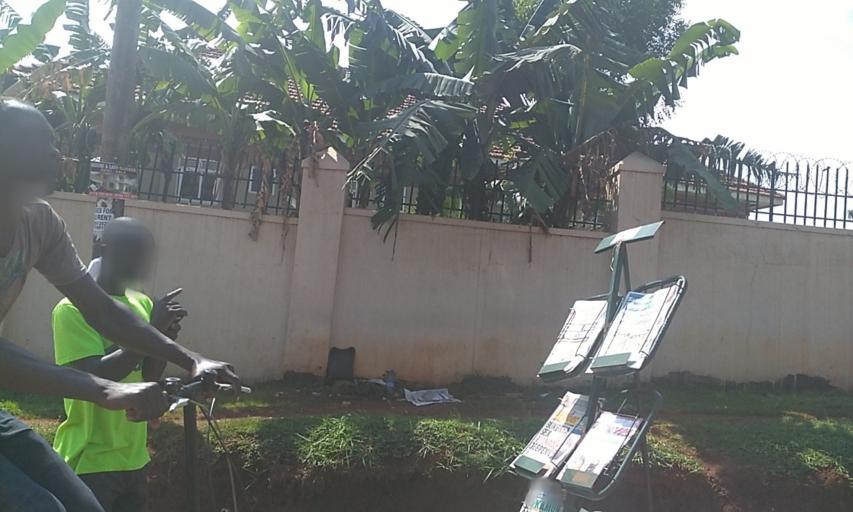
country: UG
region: Central Region
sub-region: Wakiso District
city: Kireka
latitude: 0.3568
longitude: 32.6195
